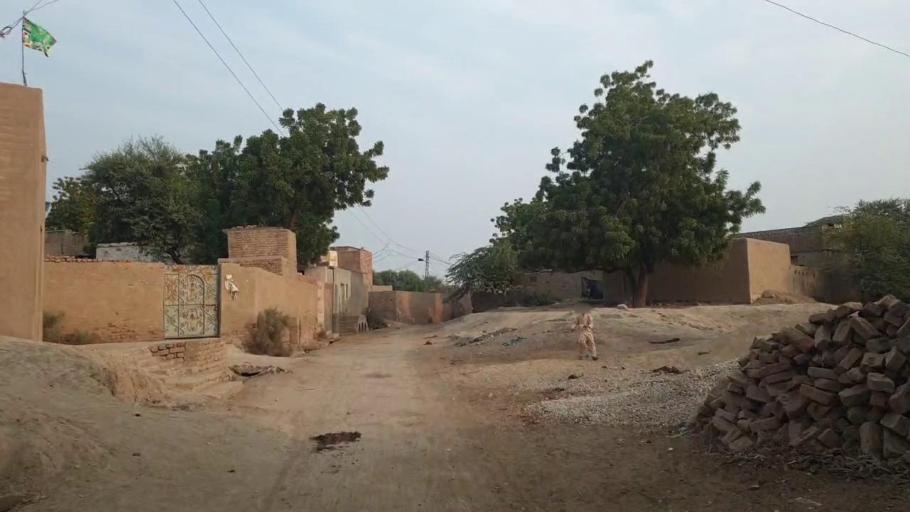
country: PK
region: Sindh
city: Sann
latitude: 26.1714
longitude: 68.0183
